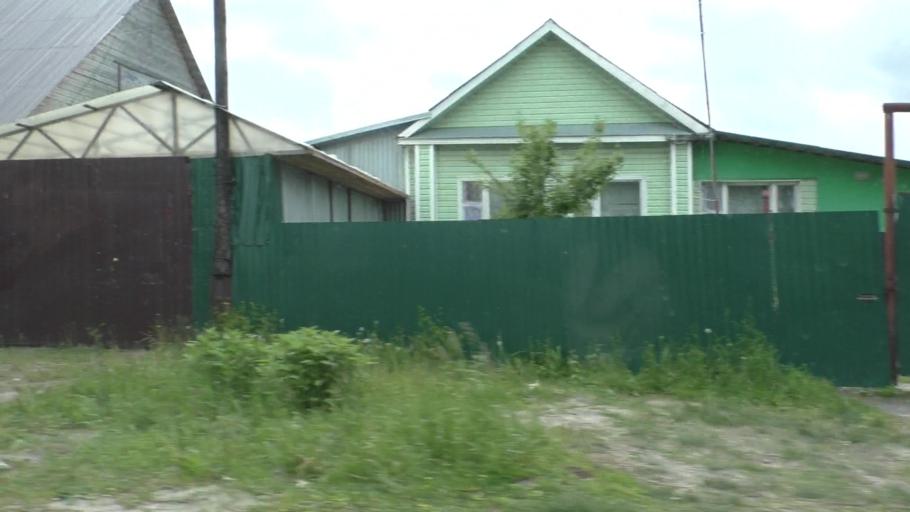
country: RU
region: Moskovskaya
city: Yegor'yevsk
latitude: 55.4000
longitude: 39.0080
